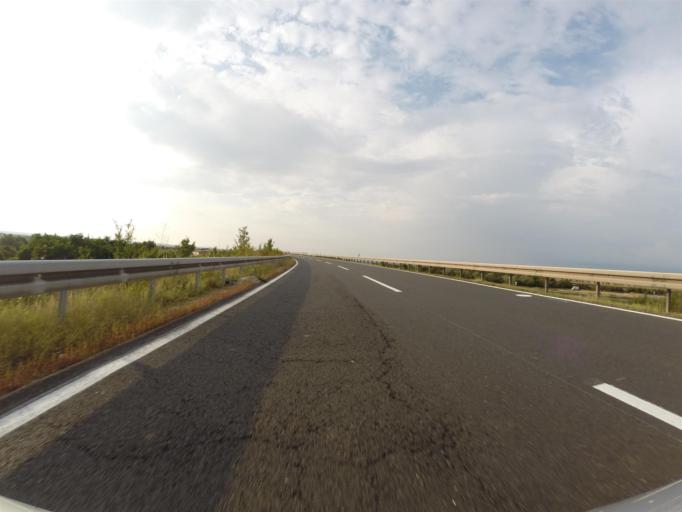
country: DE
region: Saxony-Anhalt
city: Grosskorbetha
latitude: 51.2360
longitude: 12.0563
